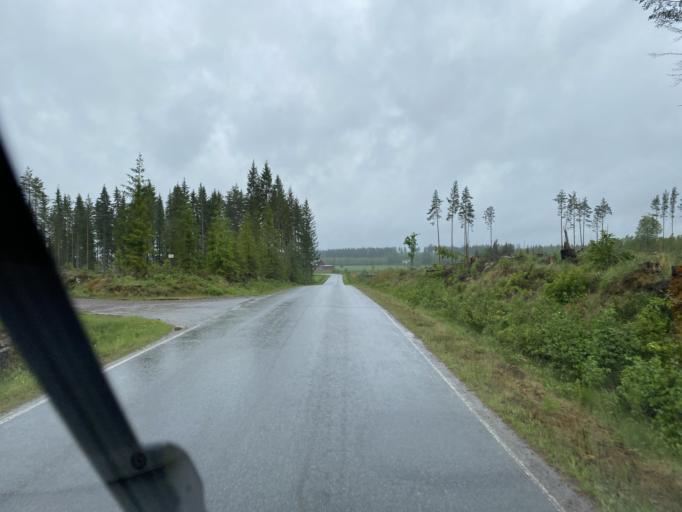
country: FI
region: Haeme
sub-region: Forssa
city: Humppila
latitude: 61.0577
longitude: 23.3256
